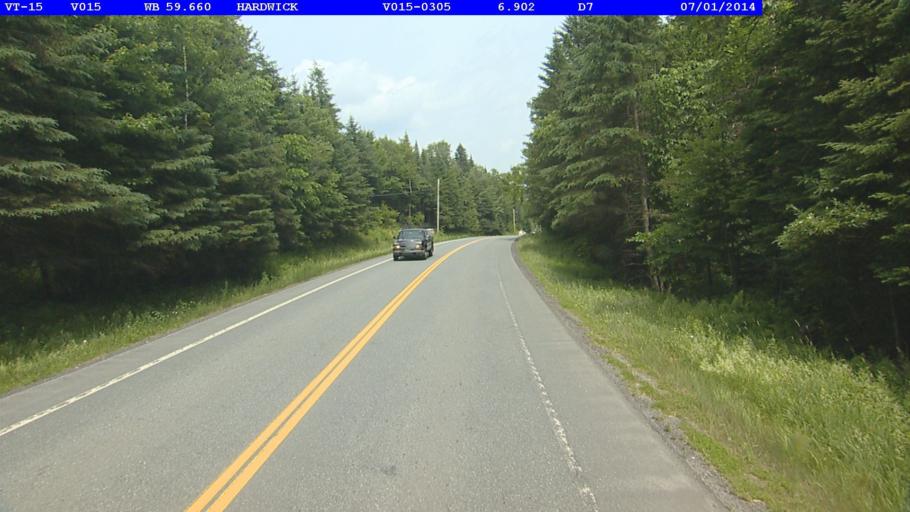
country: US
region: Vermont
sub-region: Caledonia County
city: Hardwick
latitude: 44.4875
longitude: -72.3096
